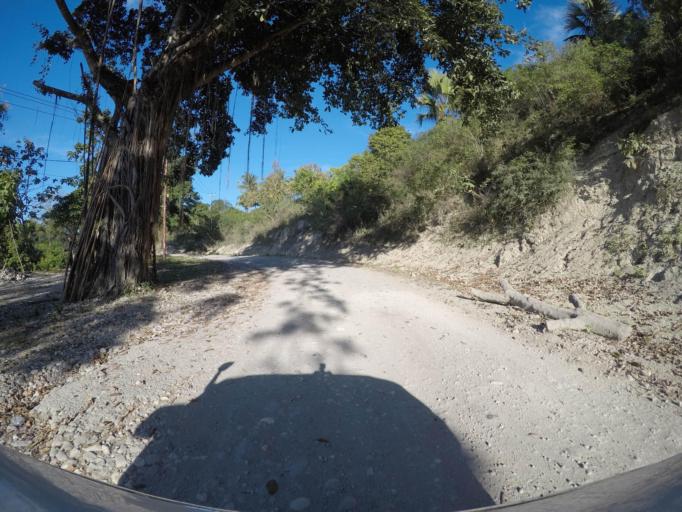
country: TL
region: Viqueque
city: Viqueque
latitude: -8.8703
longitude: 126.3455
